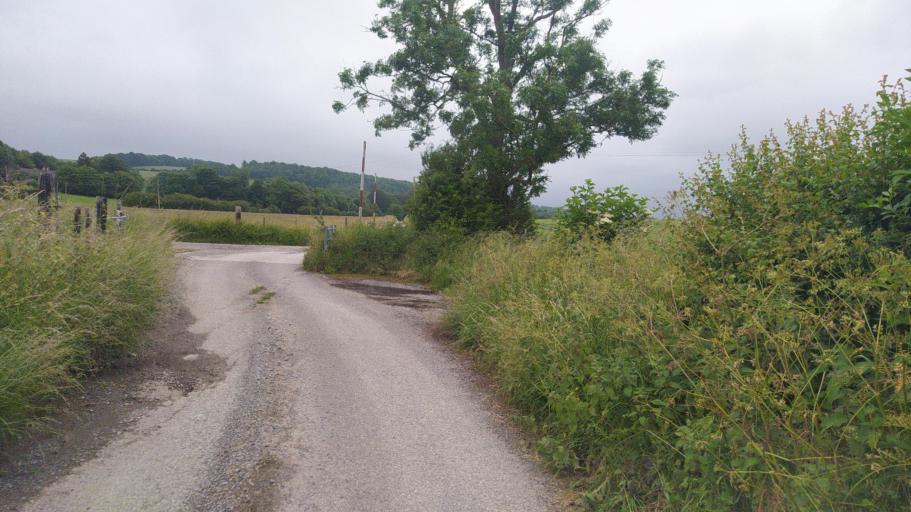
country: GB
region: England
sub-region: Wiltshire
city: Bishopstrow
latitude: 51.1995
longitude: -2.1050
